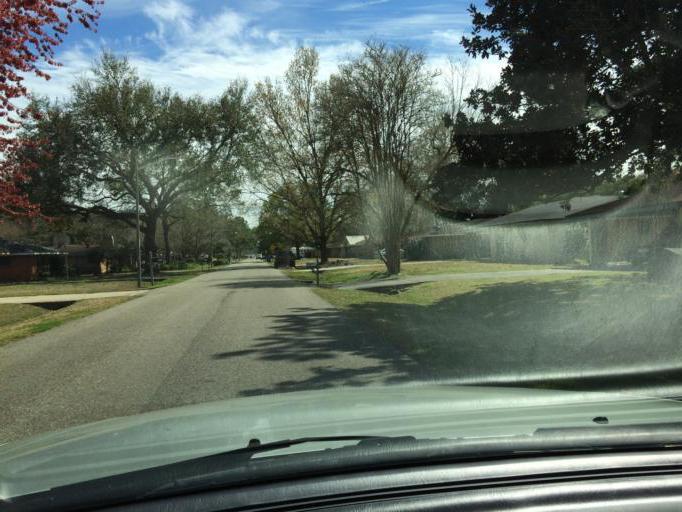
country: US
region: Louisiana
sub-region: Lafayette Parish
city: Lafayette
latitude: 30.2031
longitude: -92.0595
